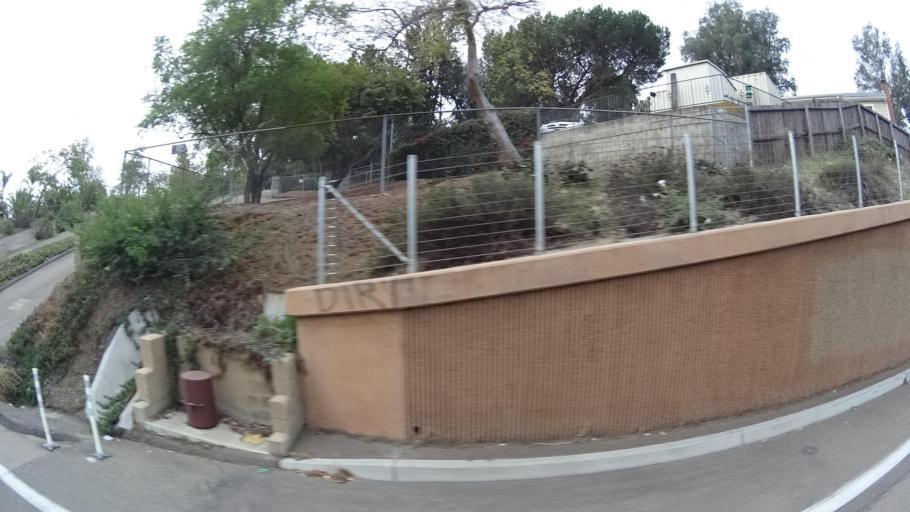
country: US
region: California
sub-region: San Diego County
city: Rancho San Diego
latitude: 32.7690
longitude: -116.9318
